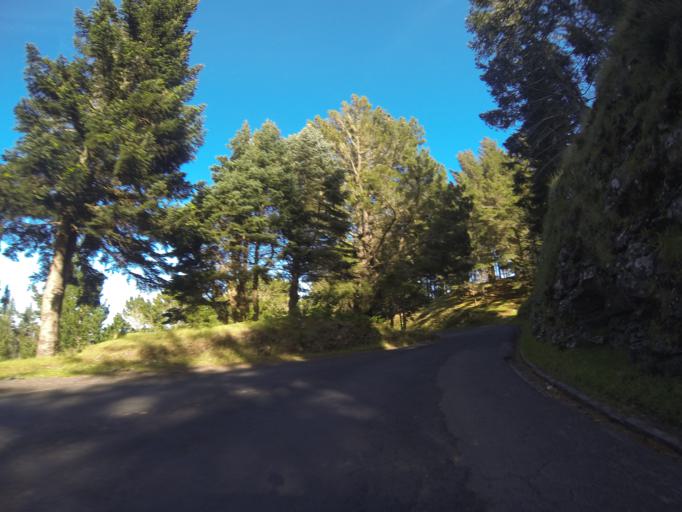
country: PT
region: Madeira
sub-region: Santa Cruz
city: Camacha
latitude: 32.6945
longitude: -16.8769
